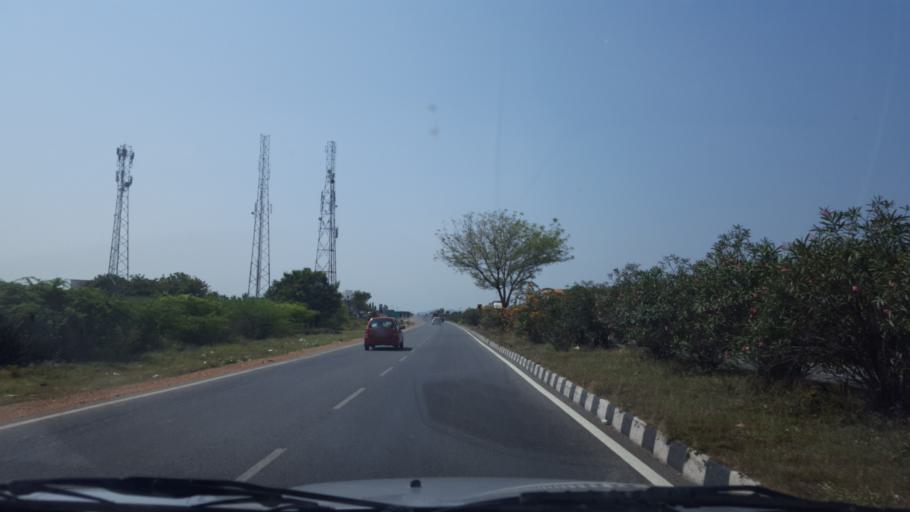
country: IN
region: Andhra Pradesh
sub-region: Guntur
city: Chilakalurupet
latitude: 16.0495
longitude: 80.1418
